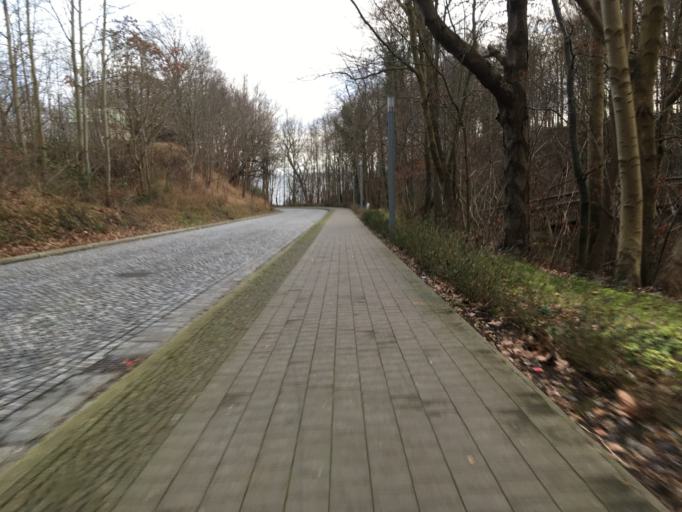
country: DE
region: Mecklenburg-Vorpommern
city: Sassnitz
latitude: 54.5079
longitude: 13.6269
